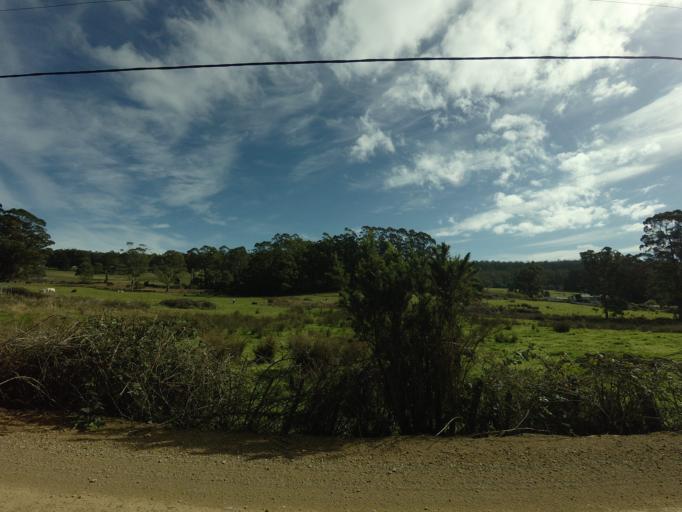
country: AU
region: Tasmania
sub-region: Clarence
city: Sandford
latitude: -43.1508
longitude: 147.7636
